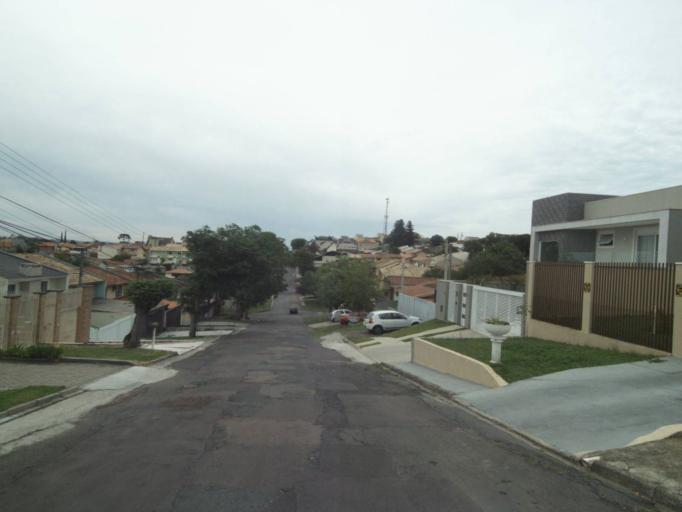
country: BR
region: Parana
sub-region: Pinhais
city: Pinhais
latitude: -25.4185
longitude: -49.2073
